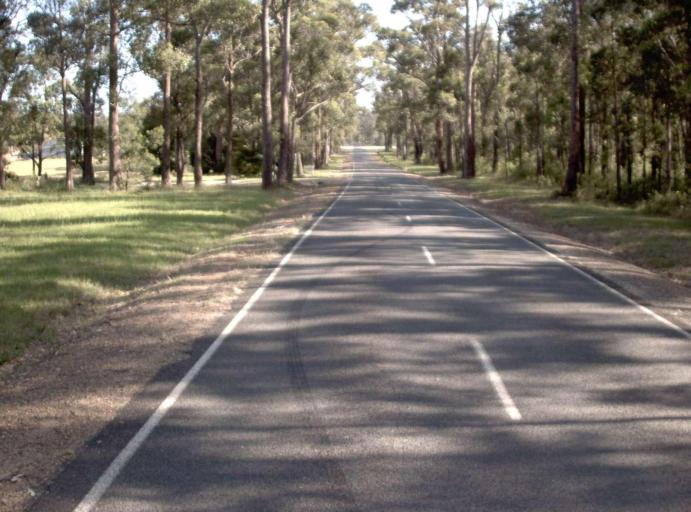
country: AU
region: Victoria
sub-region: East Gippsland
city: Lakes Entrance
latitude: -37.6813
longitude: 148.4707
